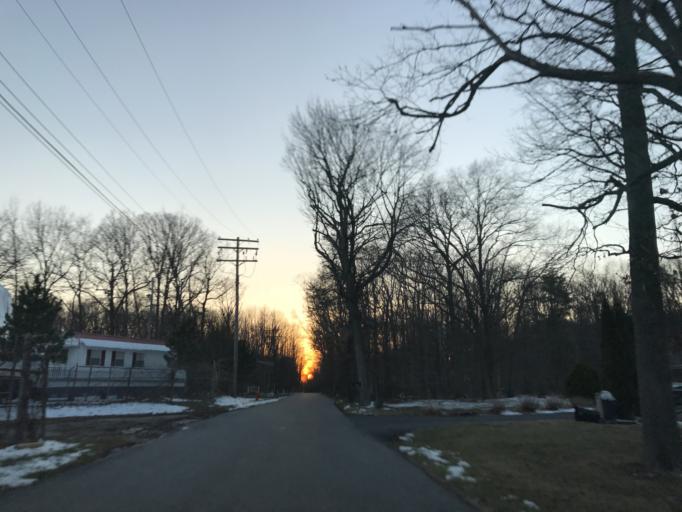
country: US
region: Maryland
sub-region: Baltimore County
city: Middle River
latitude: 39.3029
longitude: -76.4321
